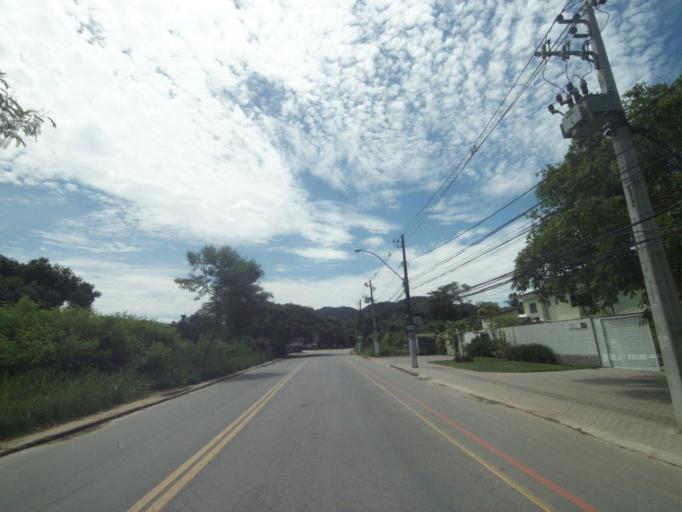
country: BR
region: Rio de Janeiro
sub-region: Niteroi
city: Niteroi
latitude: -22.9364
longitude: -43.0119
